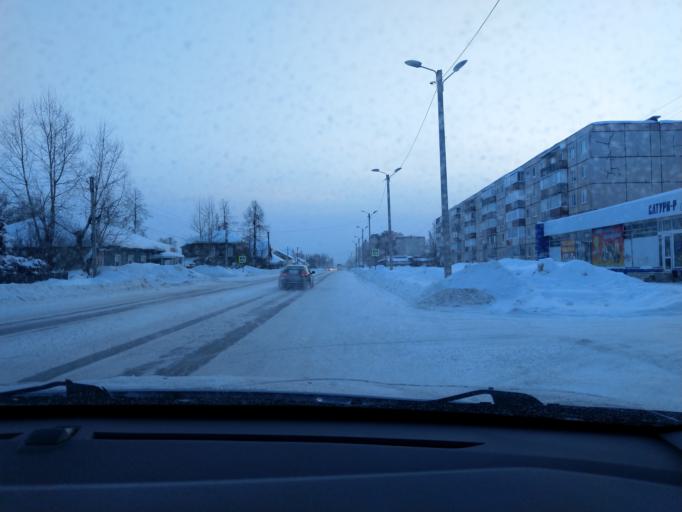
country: RU
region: Perm
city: Dobryanka
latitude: 58.4714
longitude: 56.4069
